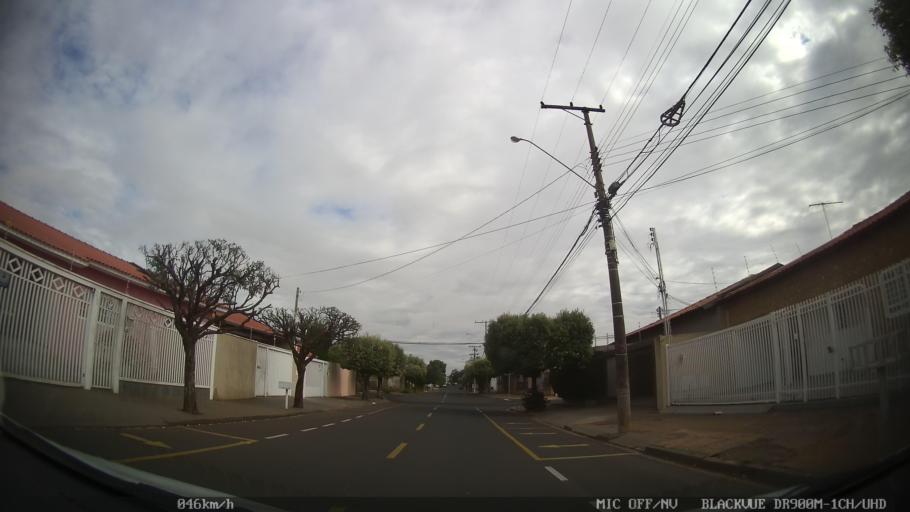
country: BR
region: Sao Paulo
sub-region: Sao Jose Do Rio Preto
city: Sao Jose do Rio Preto
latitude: -20.8168
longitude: -49.3591
